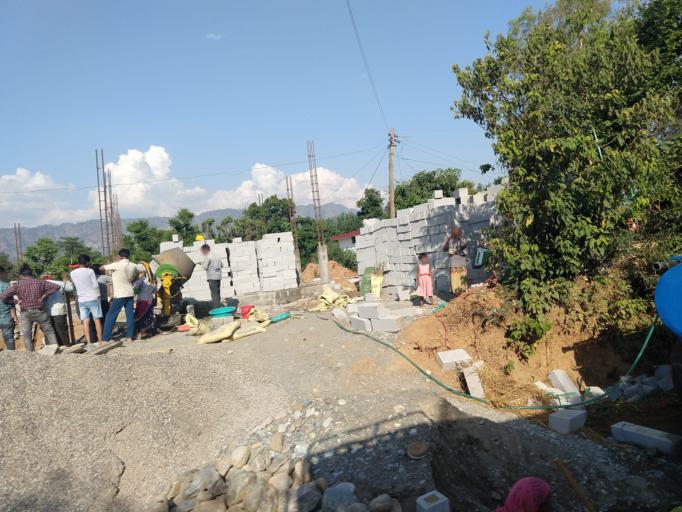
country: IN
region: Himachal Pradesh
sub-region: Chamba
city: Chowari
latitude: 32.3655
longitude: 75.9216
